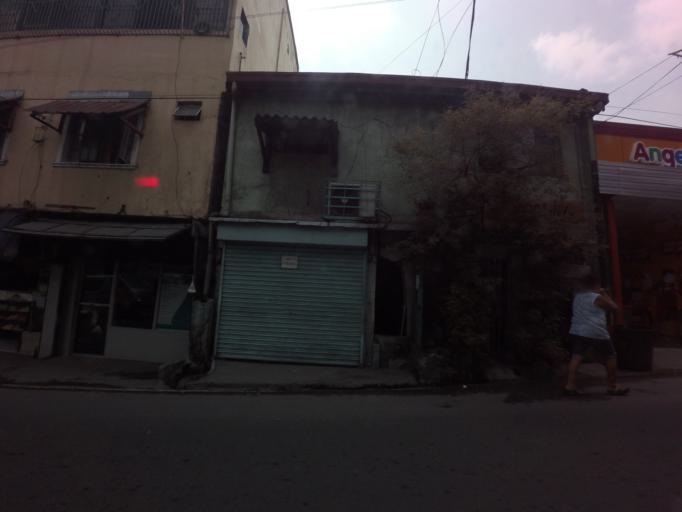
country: PH
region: Calabarzon
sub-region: Province of Rizal
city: Taguig
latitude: 14.4900
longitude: 121.0612
